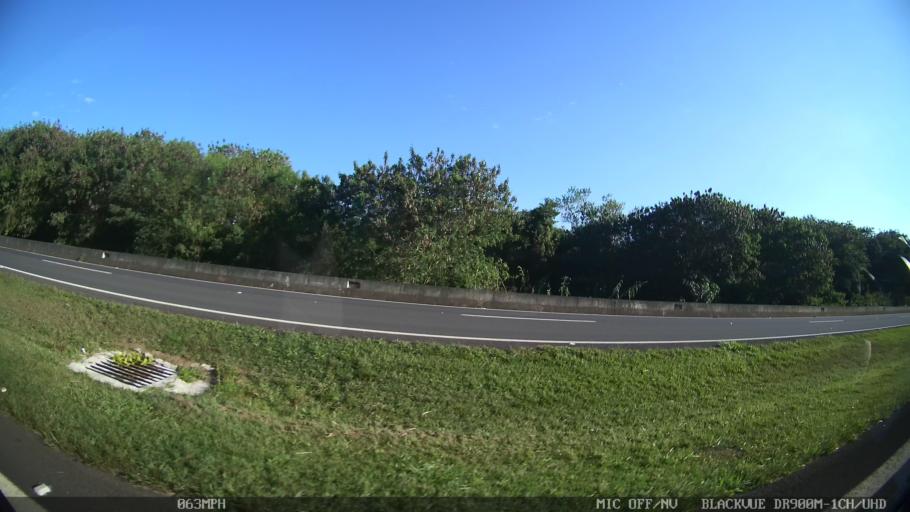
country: BR
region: Sao Paulo
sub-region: Piracicaba
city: Piracicaba
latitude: -22.6950
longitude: -47.6250
